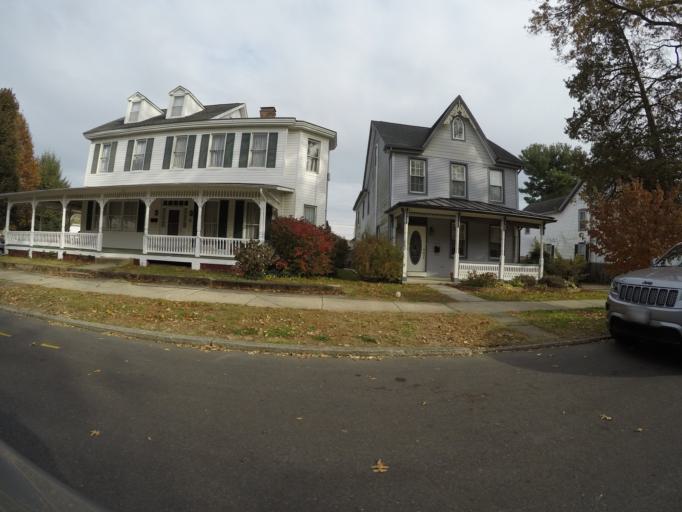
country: US
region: Maryland
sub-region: Harford County
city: Havre de Grace
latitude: 39.5453
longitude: -76.0897
